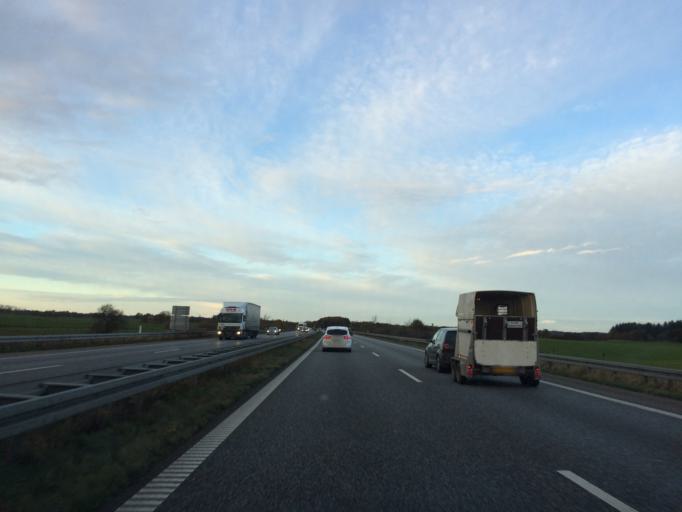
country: DK
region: South Denmark
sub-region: Aabenraa Kommune
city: Rodekro
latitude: 55.1333
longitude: 9.3756
